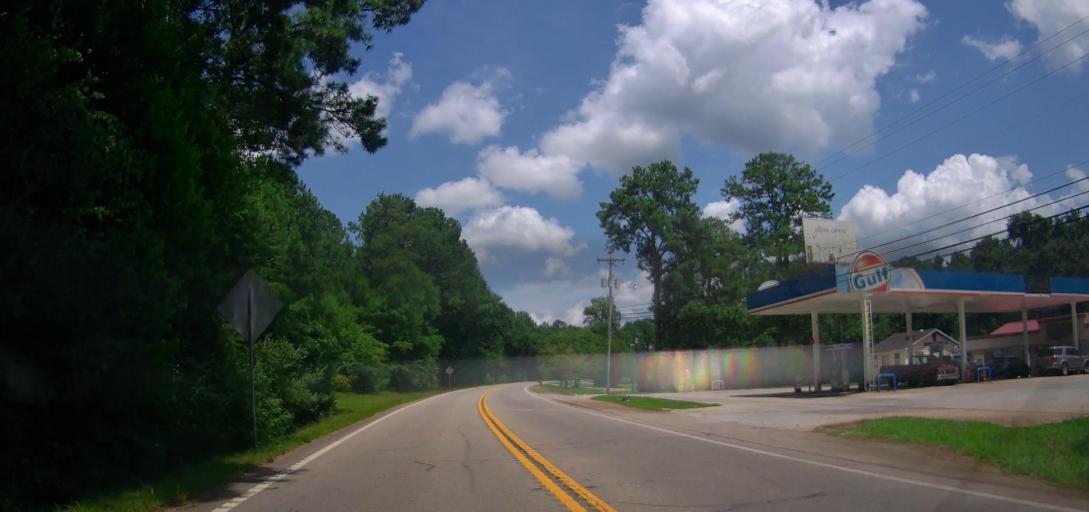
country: US
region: Georgia
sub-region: Troup County
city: Hogansville
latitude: 33.1659
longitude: -84.8892
